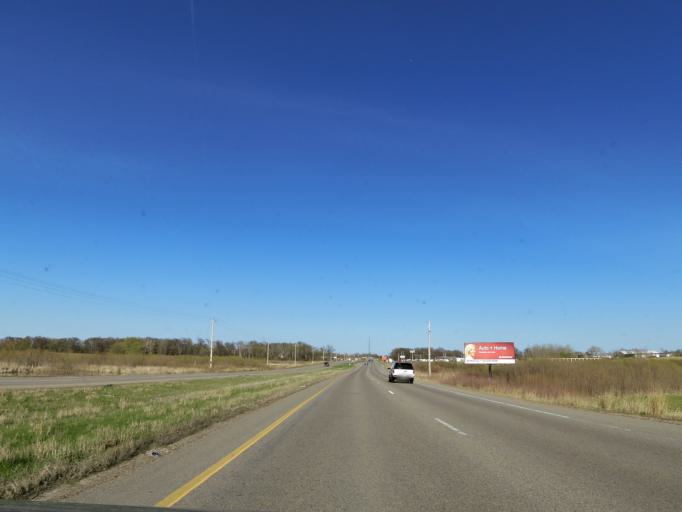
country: US
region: Minnesota
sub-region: Scott County
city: Elko New Market
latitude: 44.5733
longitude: -93.3154
